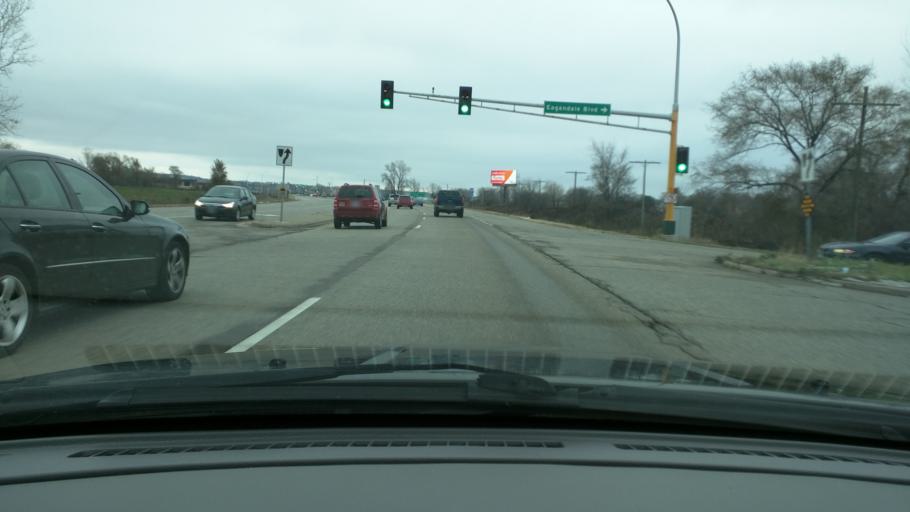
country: US
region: Minnesota
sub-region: Dakota County
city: Mendota Heights
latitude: 44.8604
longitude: -93.1489
